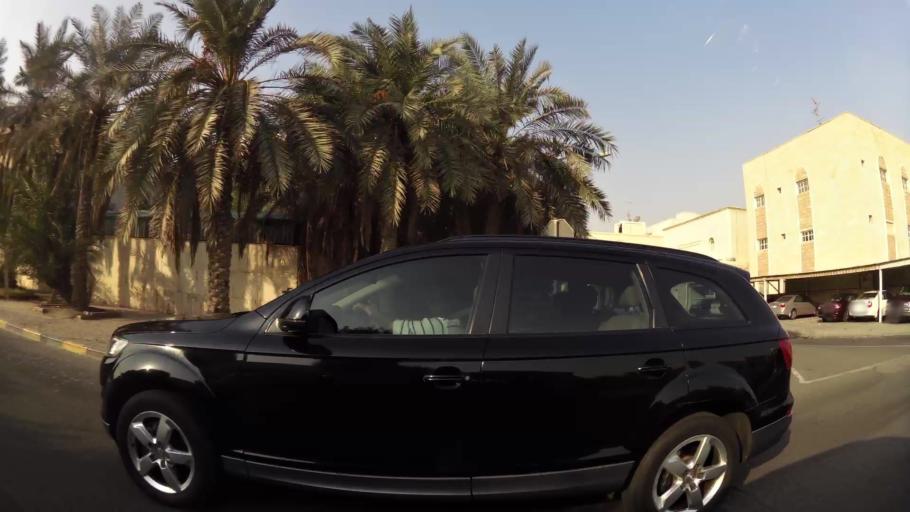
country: KW
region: Muhafazat Hawalli
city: Salwa
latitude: 29.2972
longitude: 48.0744
